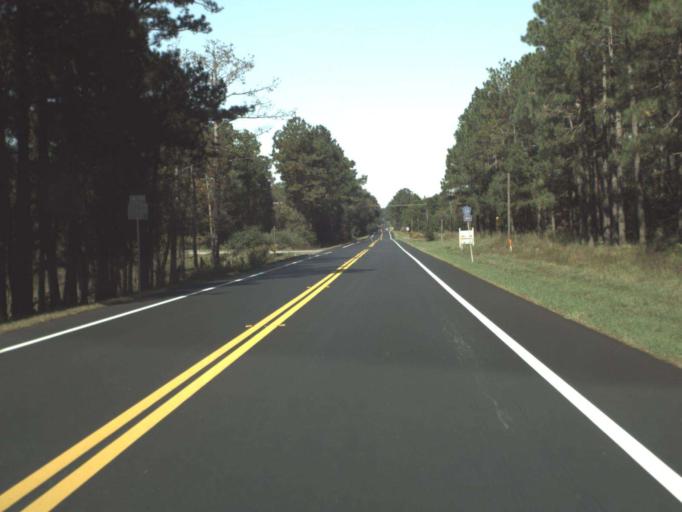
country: US
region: Alabama
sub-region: Covington County
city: Florala
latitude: 30.8521
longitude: -86.2449
